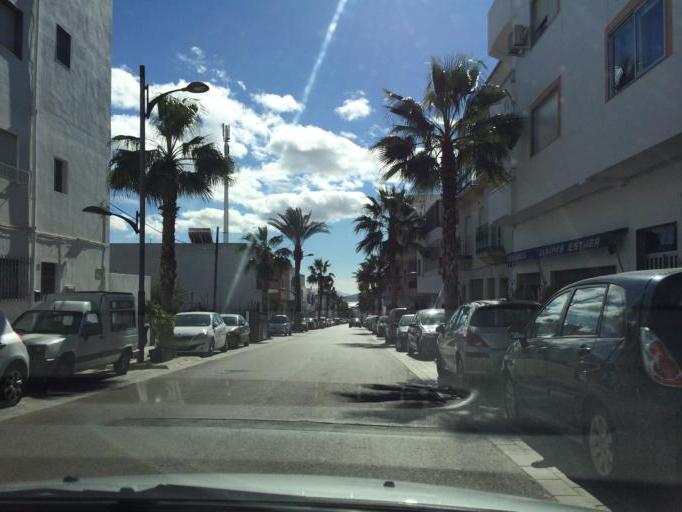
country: ES
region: Andalusia
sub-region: Provincia de Almeria
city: Nijar
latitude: 36.9634
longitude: -2.2072
